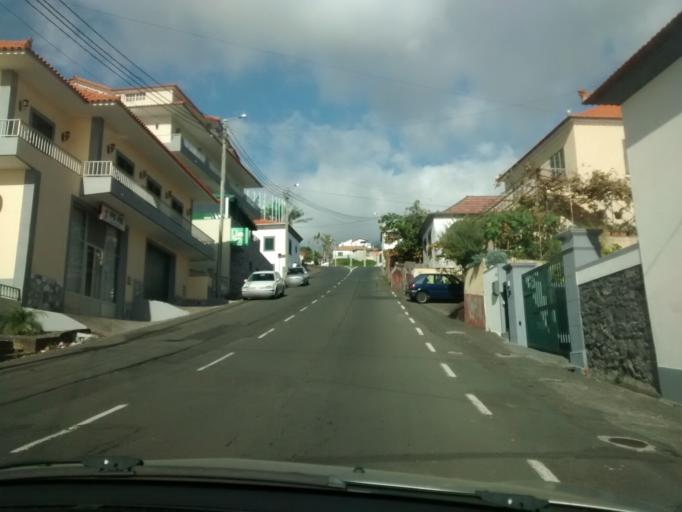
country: PT
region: Madeira
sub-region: Calheta
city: Estreito da Calheta
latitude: 32.7293
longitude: -17.1785
